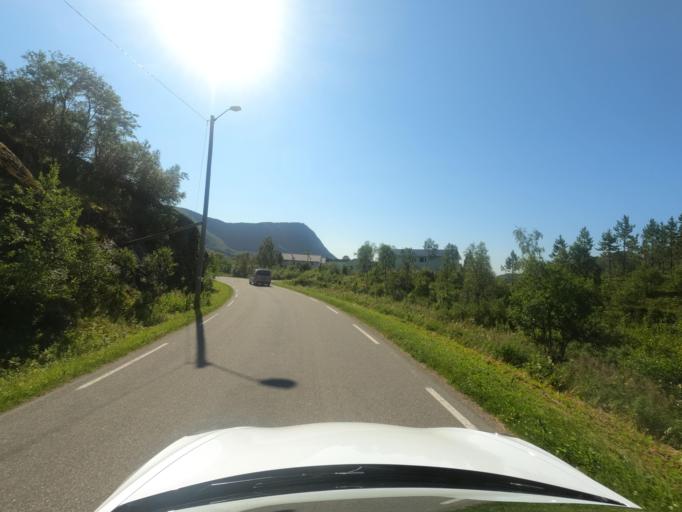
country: NO
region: Nordland
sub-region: Hadsel
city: Stokmarknes
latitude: 68.3114
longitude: 14.9869
